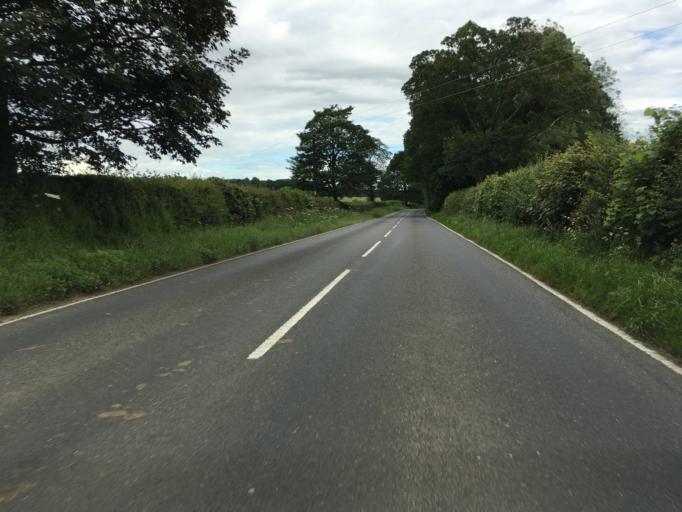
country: GB
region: England
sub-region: Central Bedfordshire
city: Potsgrove
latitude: 51.9703
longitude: -0.6428
